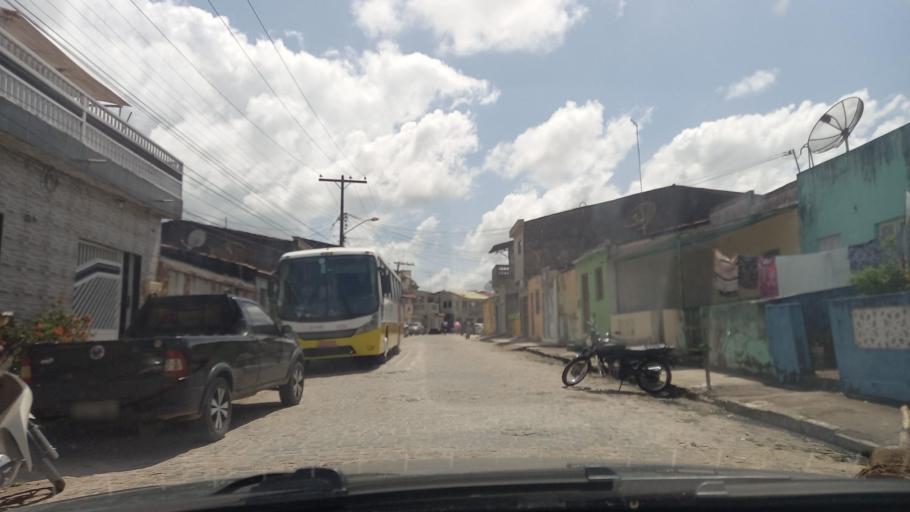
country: BR
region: Pernambuco
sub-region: Goiana
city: Goiana
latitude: -7.5636
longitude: -35.0081
